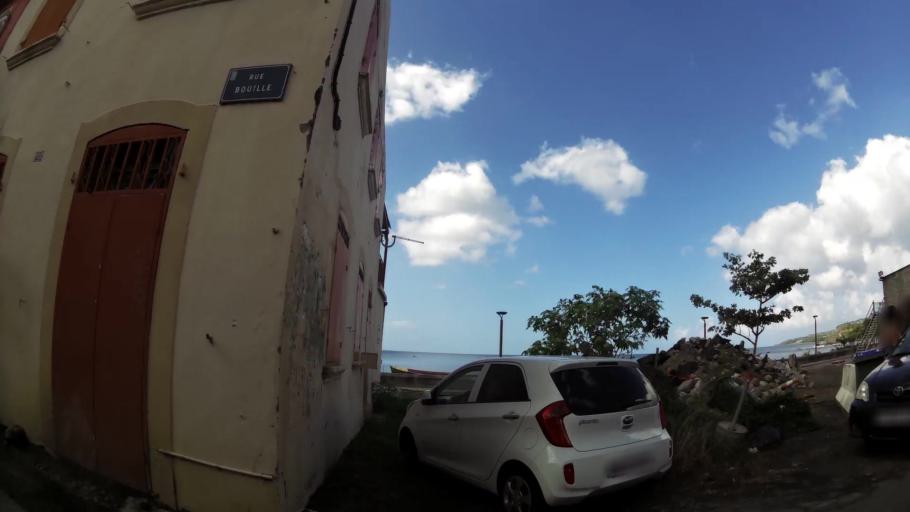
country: MQ
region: Martinique
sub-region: Martinique
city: Saint-Pierre
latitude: 14.7443
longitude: -61.1762
